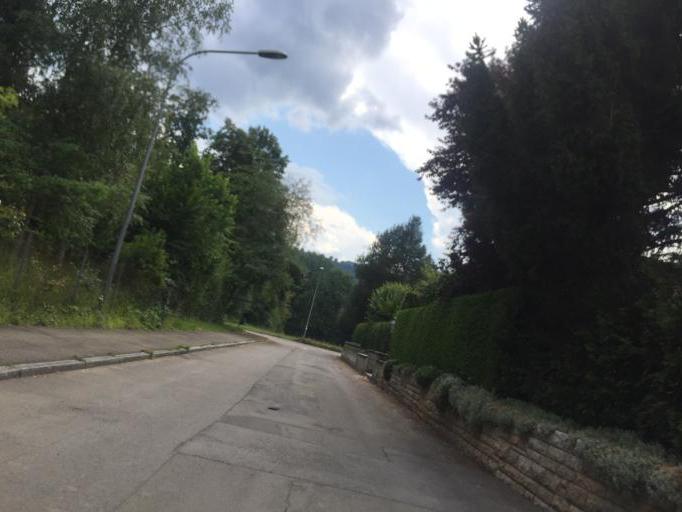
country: CH
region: Bern
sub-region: Bern-Mittelland District
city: Muri
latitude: 46.9283
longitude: 7.4730
